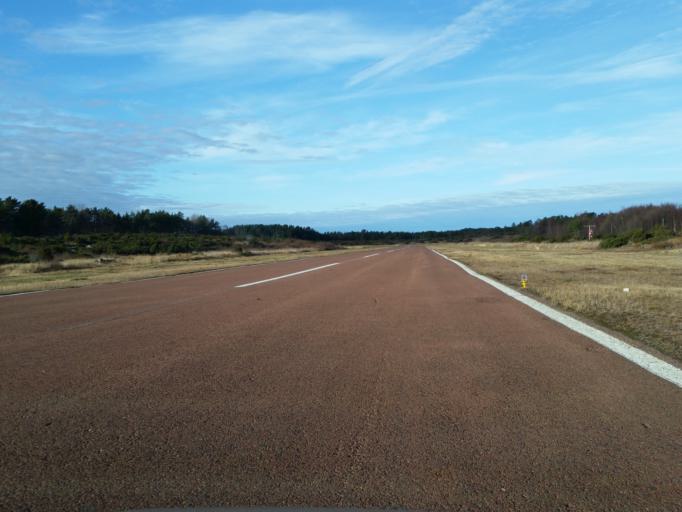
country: AX
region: Alands skaergard
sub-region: Kumlinge
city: Kumlinge
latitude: 60.2431
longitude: 20.8062
